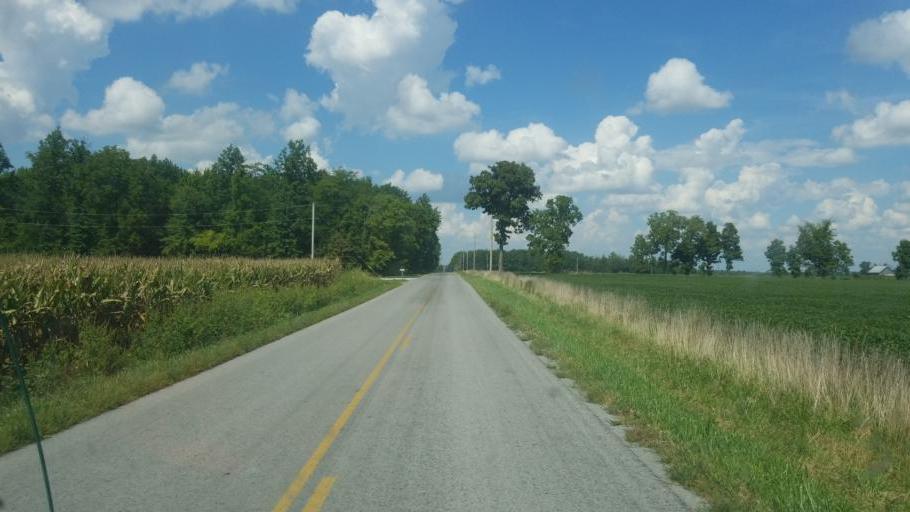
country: US
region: Ohio
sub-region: Wyandot County
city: Carey
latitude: 40.8717
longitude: -83.4192
